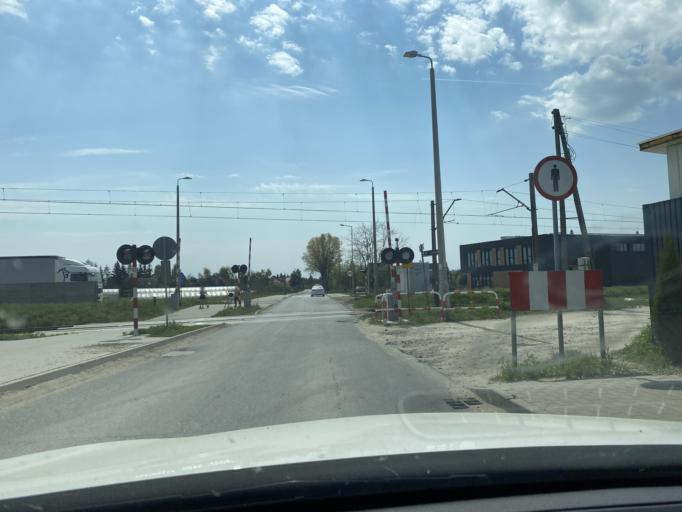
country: PL
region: Lower Silesian Voivodeship
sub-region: Powiat wroclawski
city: Mirkow
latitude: 51.1654
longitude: 17.1645
